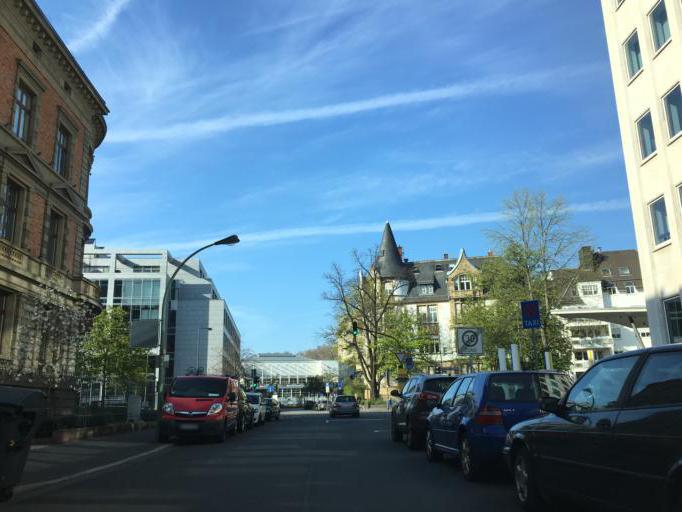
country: DE
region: Hesse
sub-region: Regierungsbezirk Darmstadt
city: Frankfurt am Main
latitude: 50.1193
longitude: 8.6567
